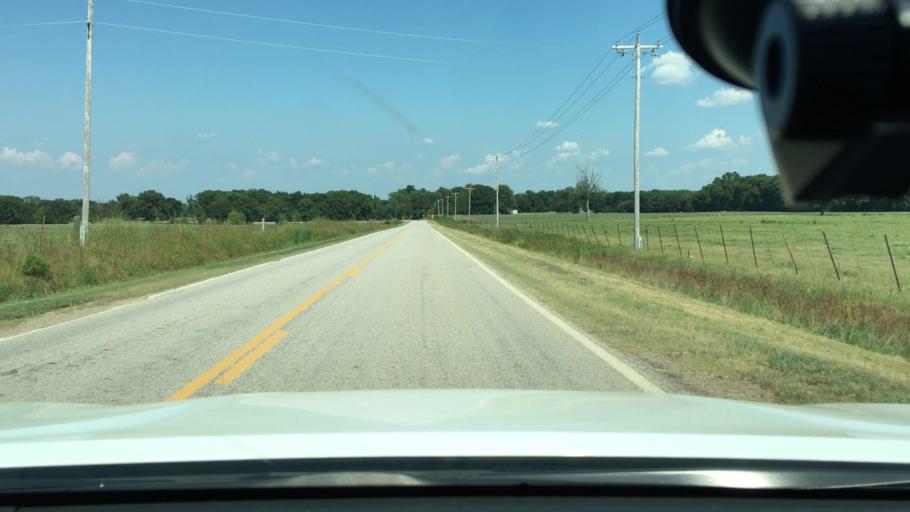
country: US
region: Arkansas
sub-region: Johnson County
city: Coal Hill
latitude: 35.3508
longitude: -93.5735
